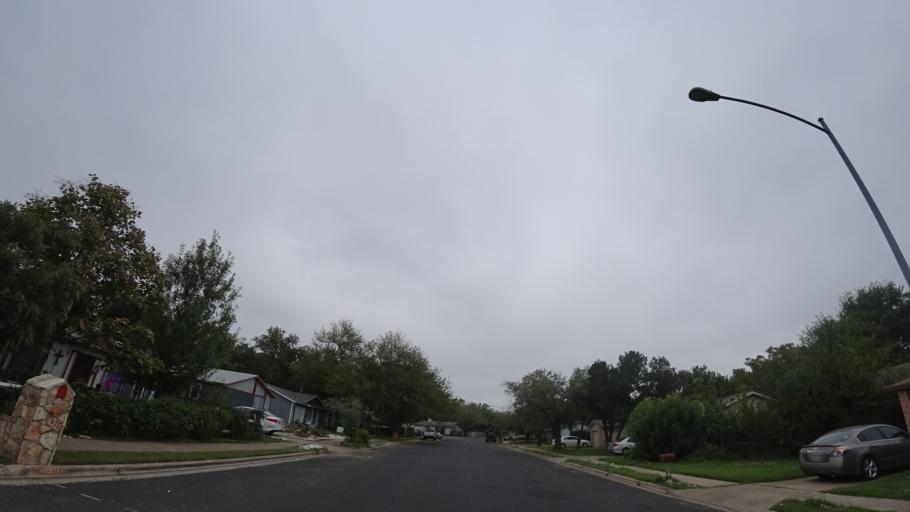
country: US
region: Texas
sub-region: Travis County
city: Onion Creek
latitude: 30.2007
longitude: -97.7805
